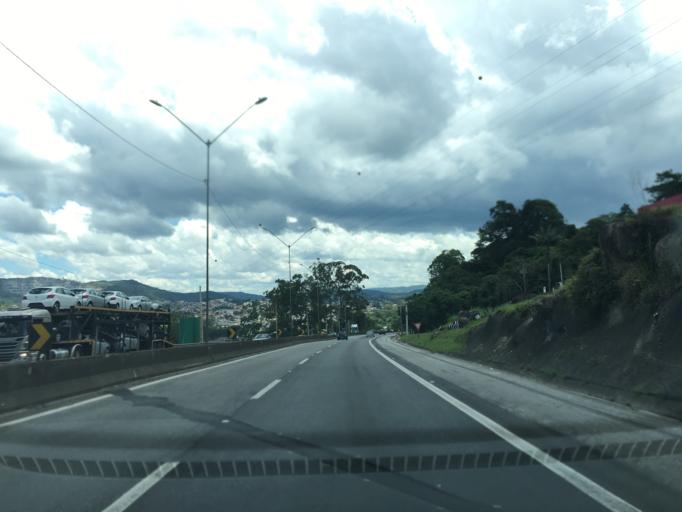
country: BR
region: Sao Paulo
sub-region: Mairipora
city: Mairipora
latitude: -23.3051
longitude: -46.5744
